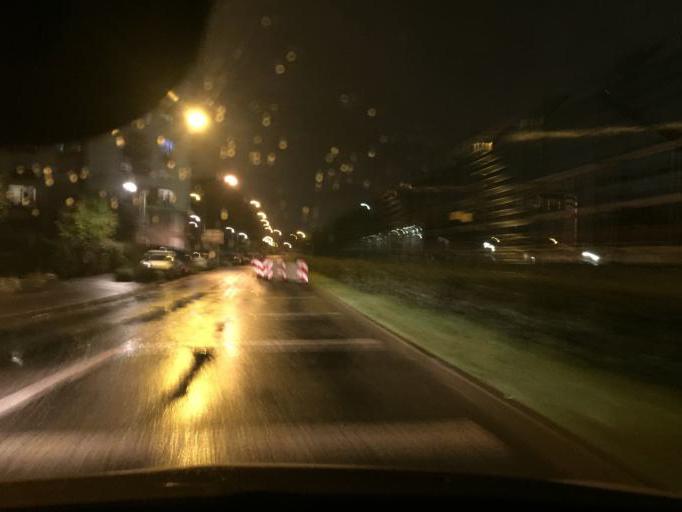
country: FR
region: Ile-de-France
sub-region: Departement du Val-de-Marne
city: Bonneuil-sur-Marne
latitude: 48.7683
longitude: 2.4651
